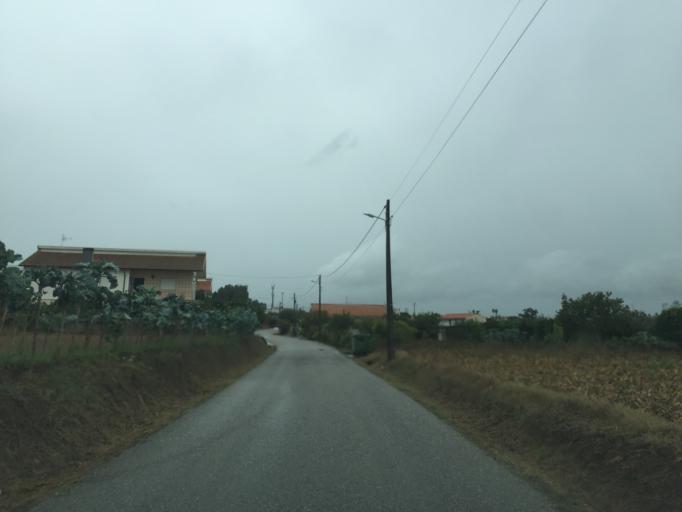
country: PT
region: Coimbra
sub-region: Figueira da Foz
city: Lavos
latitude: 40.0601
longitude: -8.8104
